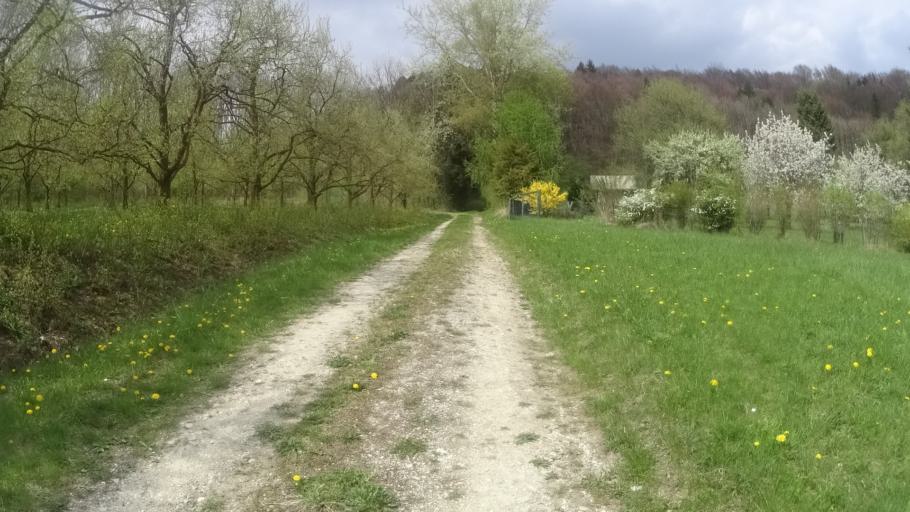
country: DE
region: Bavaria
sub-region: Upper Franconia
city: Kleinsendelbach
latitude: 49.6238
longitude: 11.1834
